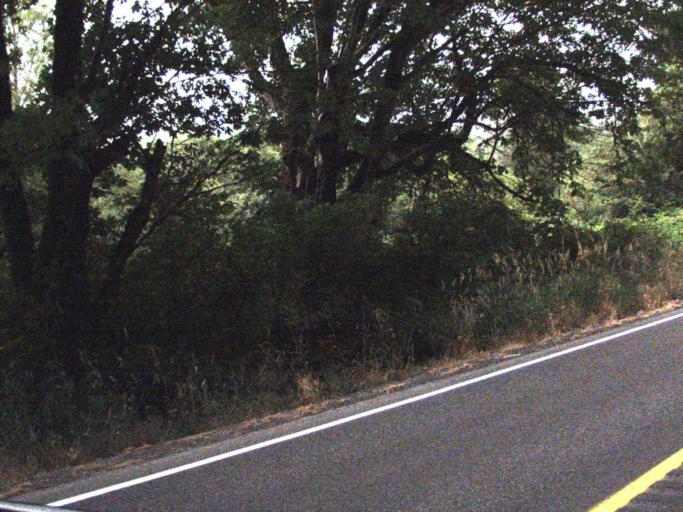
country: US
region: Washington
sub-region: King County
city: Lake Marcel-Stillwater
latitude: 47.6933
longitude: -121.9671
